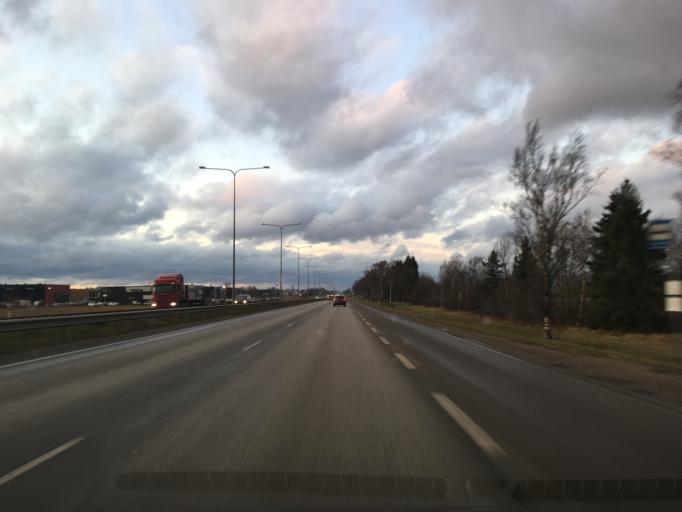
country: EE
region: Harju
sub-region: Rae vald
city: Jueri
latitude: 59.3893
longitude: 24.8293
